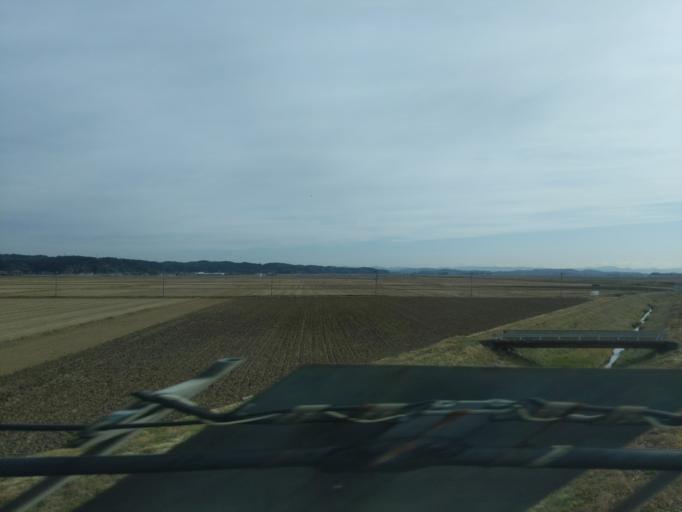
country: JP
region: Iwate
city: Ichinoseki
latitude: 38.8000
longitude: 141.0963
